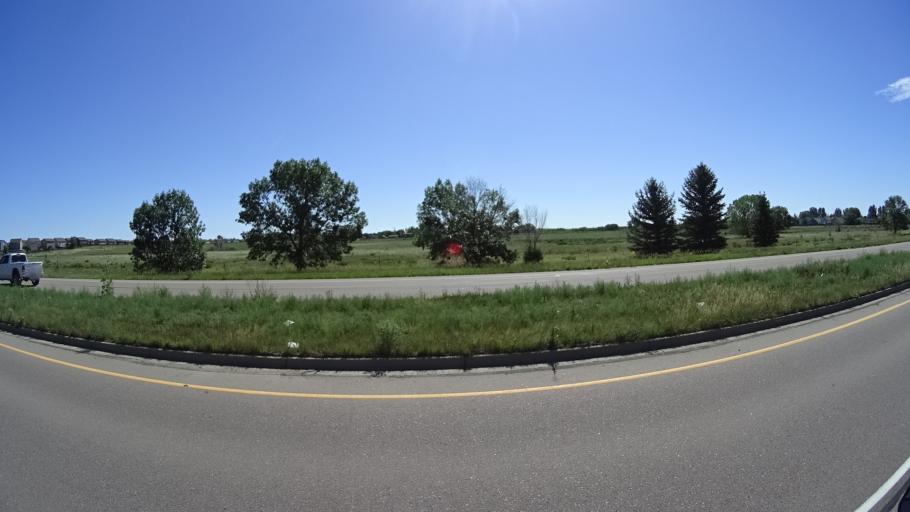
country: US
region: Colorado
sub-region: El Paso County
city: Security-Widefield
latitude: 38.7721
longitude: -104.6598
